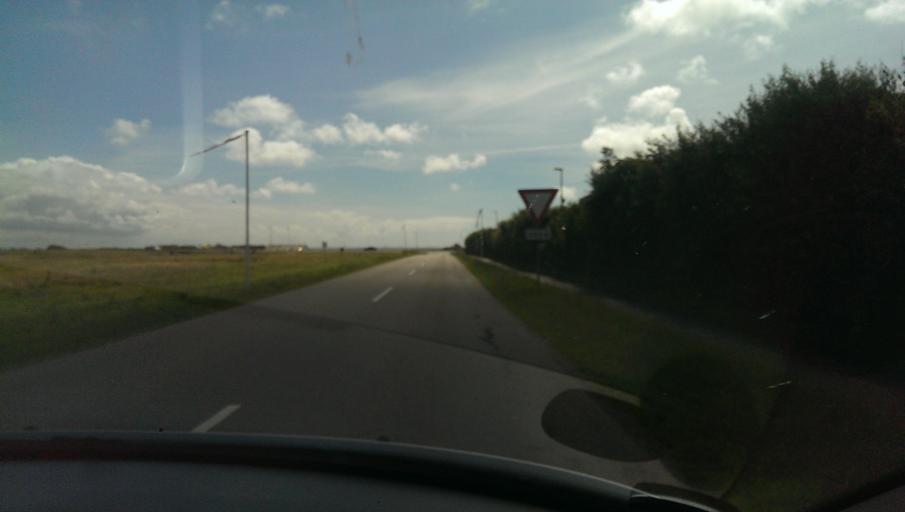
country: DK
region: Central Jutland
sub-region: Ringkobing-Skjern Kommune
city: Ringkobing
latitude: 56.1173
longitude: 8.1758
